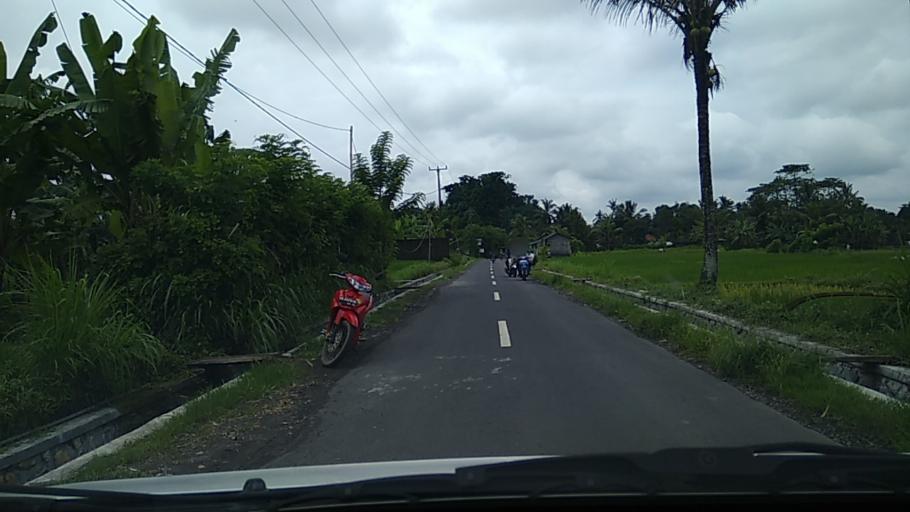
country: ID
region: Bali
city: Brahmana
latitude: -8.4753
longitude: 115.2014
